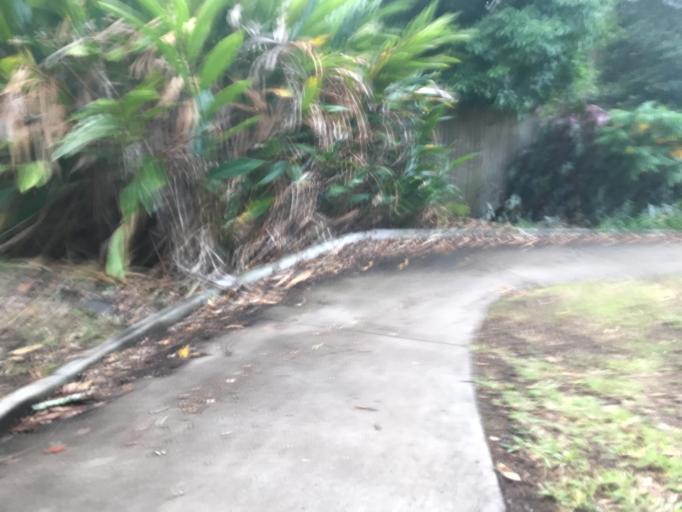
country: AU
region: Queensland
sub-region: Moreton Bay
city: Ferny Hills
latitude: -27.4399
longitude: 152.9268
